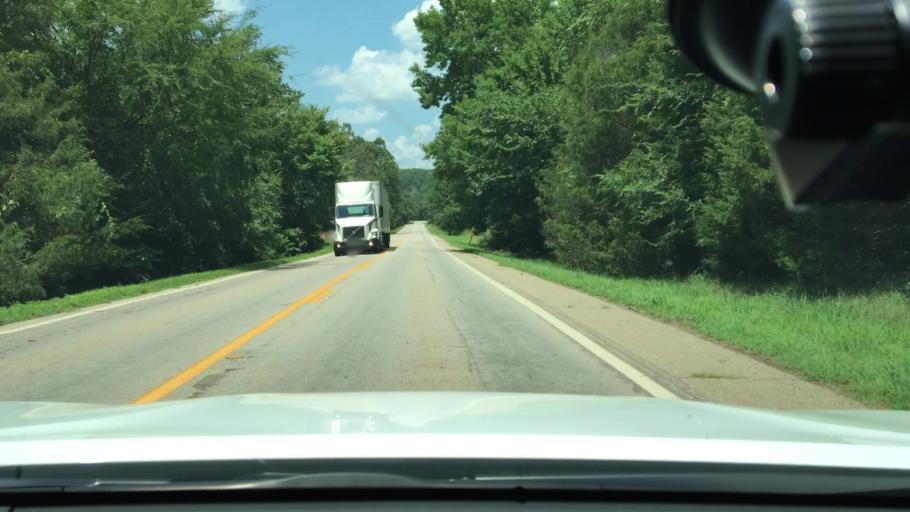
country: US
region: Arkansas
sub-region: Logan County
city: Booneville
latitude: 35.2121
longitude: -93.9331
